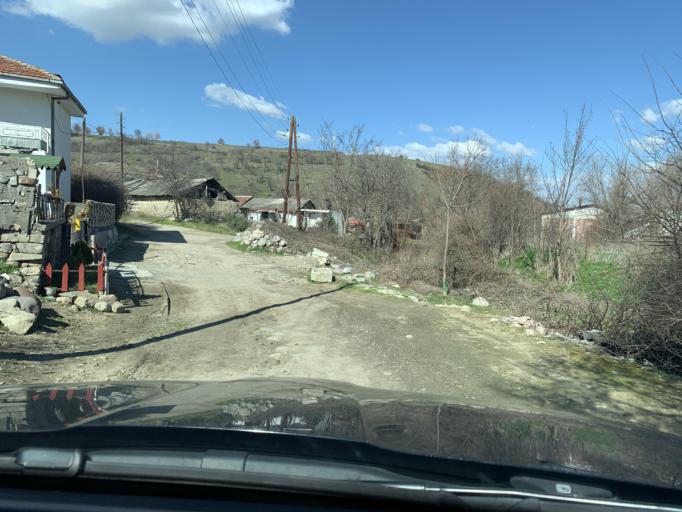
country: MK
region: Demir Kapija
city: Demir Kapija
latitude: 41.4189
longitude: 22.1660
